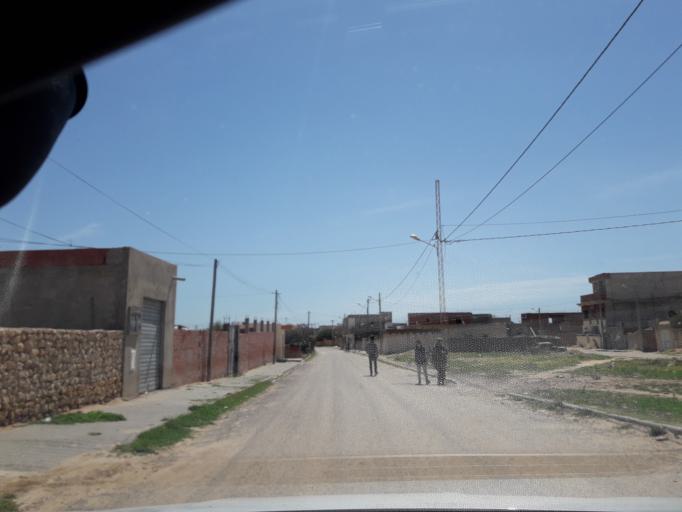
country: TN
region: Safaqis
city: Sfax
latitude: 34.7428
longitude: 10.5192
